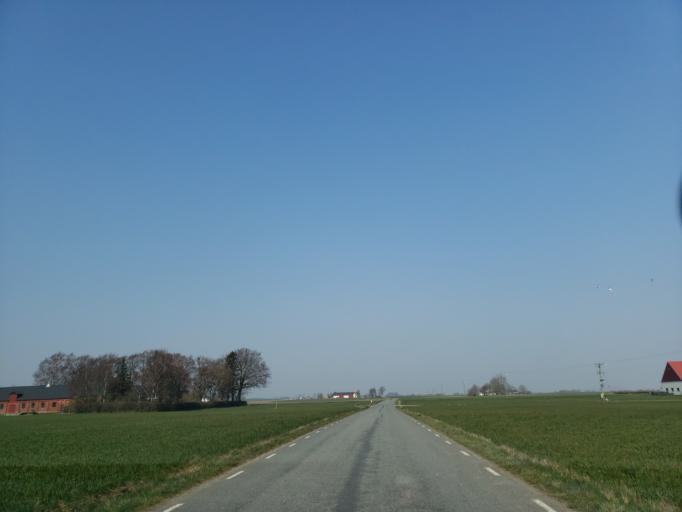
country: SE
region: Skane
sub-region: Simrishamns Kommun
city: Simrishamn
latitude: 55.4517
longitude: 14.2156
